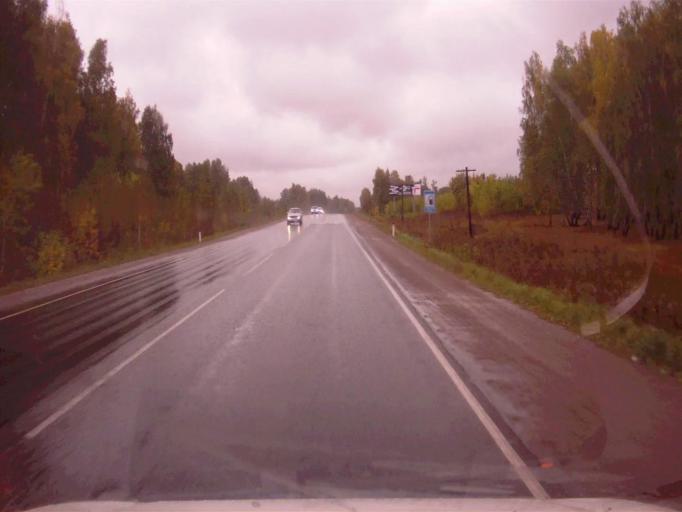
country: RU
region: Chelyabinsk
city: Argayash
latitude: 55.4683
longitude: 60.9068
